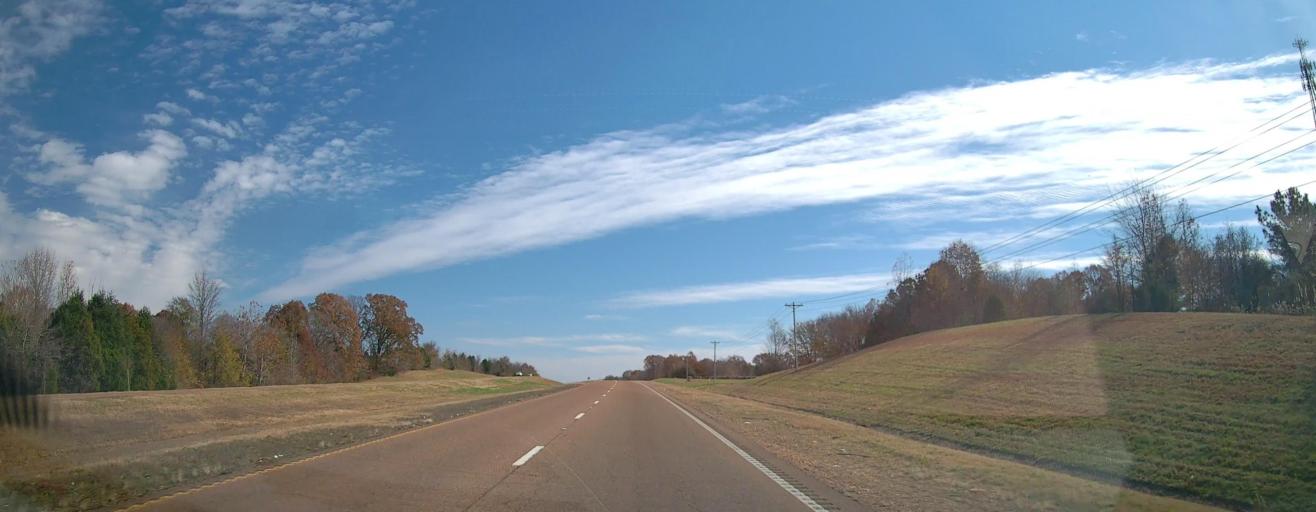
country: US
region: Tennessee
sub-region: Fayette County
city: Piperton
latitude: 34.9598
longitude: -89.5266
